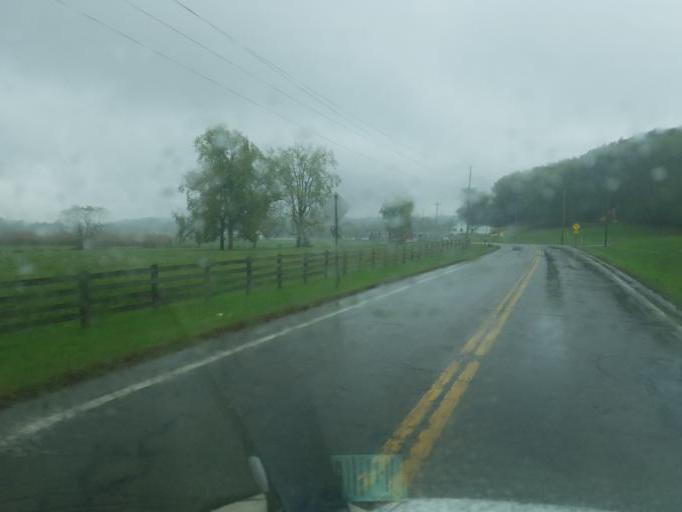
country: US
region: Ohio
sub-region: Holmes County
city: Millersburg
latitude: 40.5758
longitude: -81.9218
